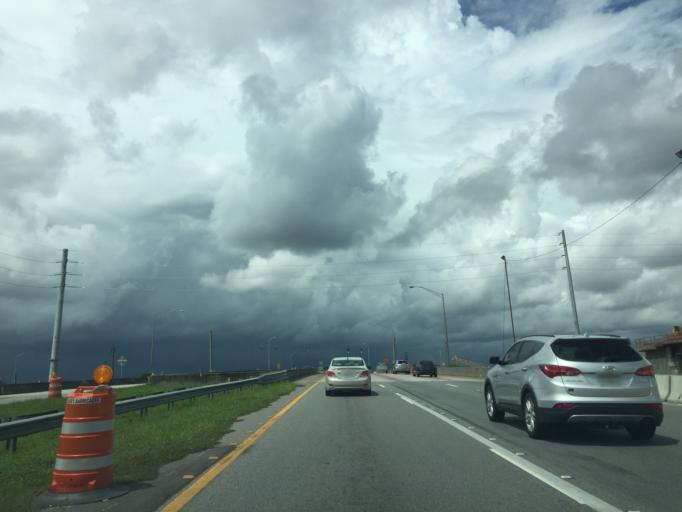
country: US
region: Florida
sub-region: Orange County
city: Eatonville
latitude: 28.6309
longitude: -81.3845
